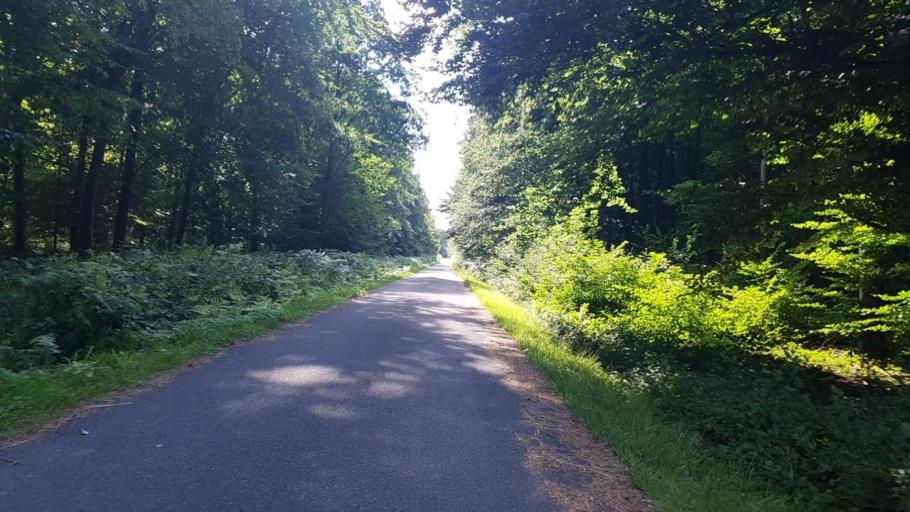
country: FR
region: Picardie
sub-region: Departement de l'Oise
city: Ver-sur-Launette
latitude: 49.1135
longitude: 2.6627
